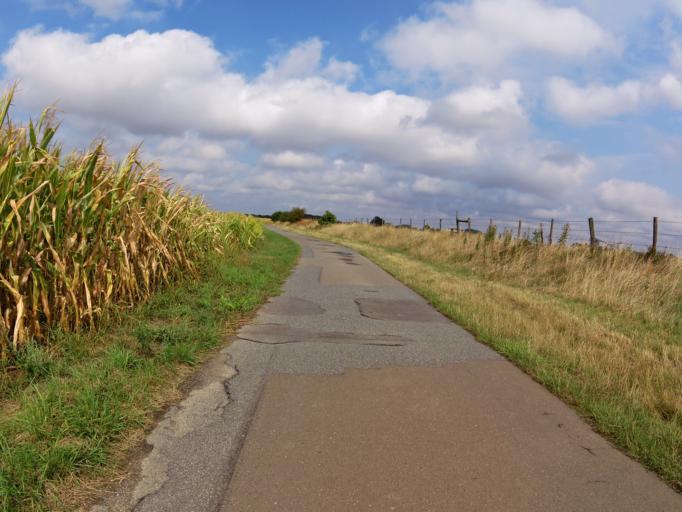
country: DE
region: Lower Saxony
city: Schweringen
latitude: 52.7540
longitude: 9.1795
